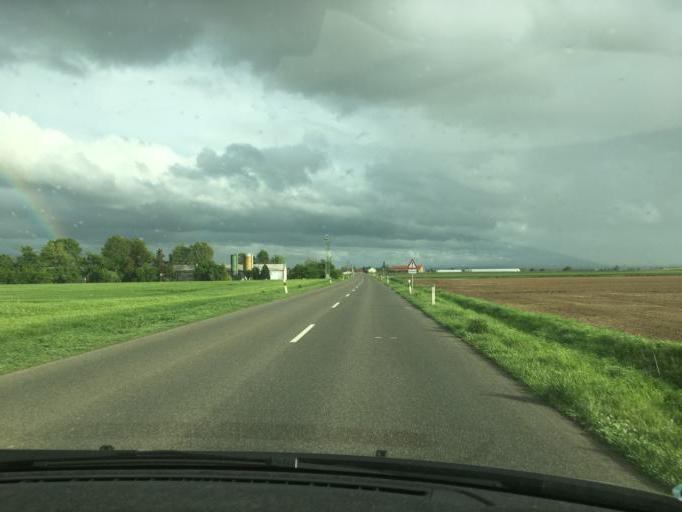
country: DE
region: North Rhine-Westphalia
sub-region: Regierungsbezirk Koln
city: Merzenich
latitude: 50.8056
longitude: 6.5608
